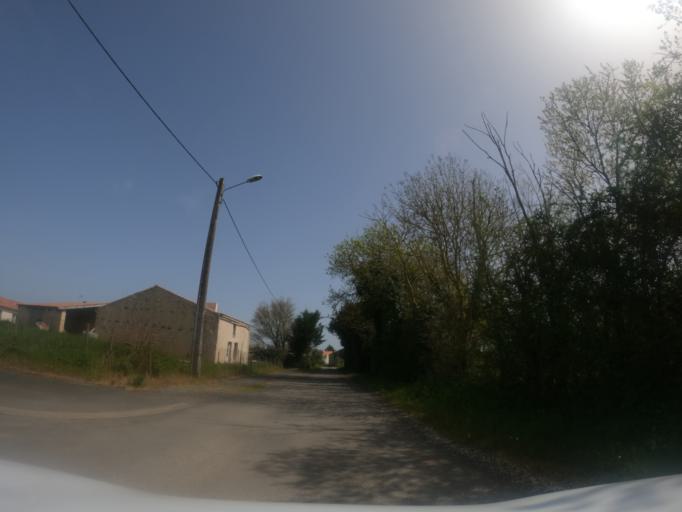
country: FR
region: Pays de la Loire
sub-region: Departement de la Vendee
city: Vix
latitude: 46.3880
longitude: -0.8109
